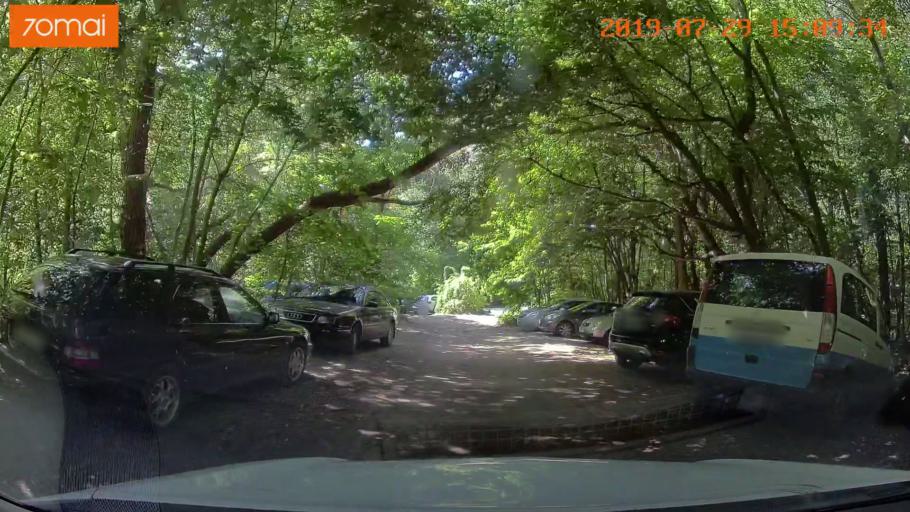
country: RU
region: Kaliningrad
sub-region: Gorod Kaliningrad
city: Baltiysk
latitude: 54.6812
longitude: 19.9150
